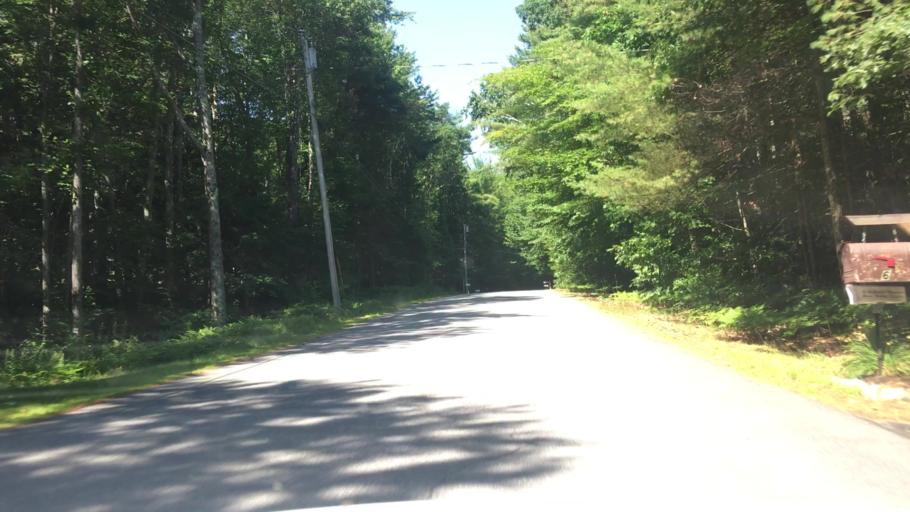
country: US
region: Maine
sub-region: Cumberland County
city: Cumberland Center
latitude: 43.8012
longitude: -70.3320
